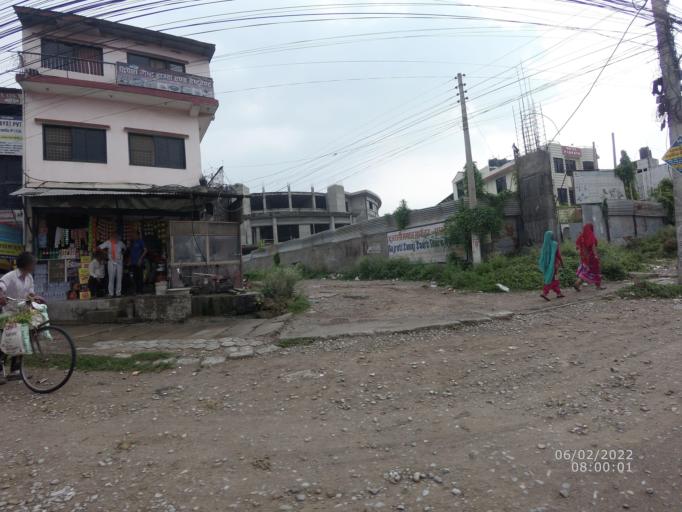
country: NP
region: Western Region
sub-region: Lumbini Zone
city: Bhairahawa
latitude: 27.4788
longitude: 83.4690
